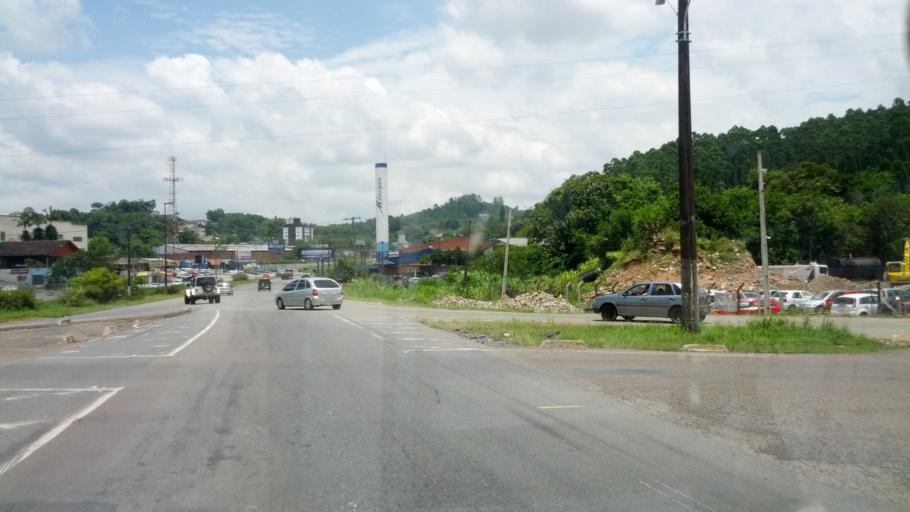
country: BR
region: Santa Catarina
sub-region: Blumenau
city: Blumenau
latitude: -26.8731
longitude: -49.1140
